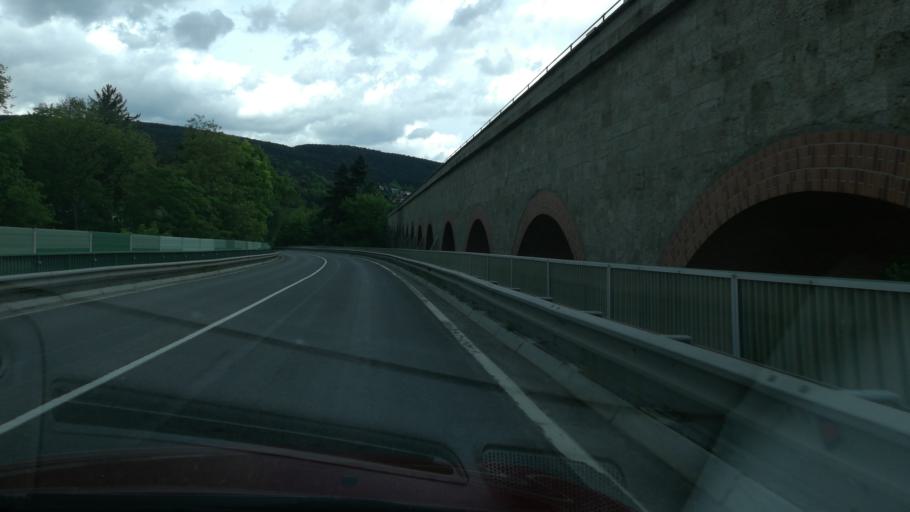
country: AT
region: Lower Austria
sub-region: Politischer Bezirk Baden
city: Baden
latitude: 48.0037
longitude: 16.2119
